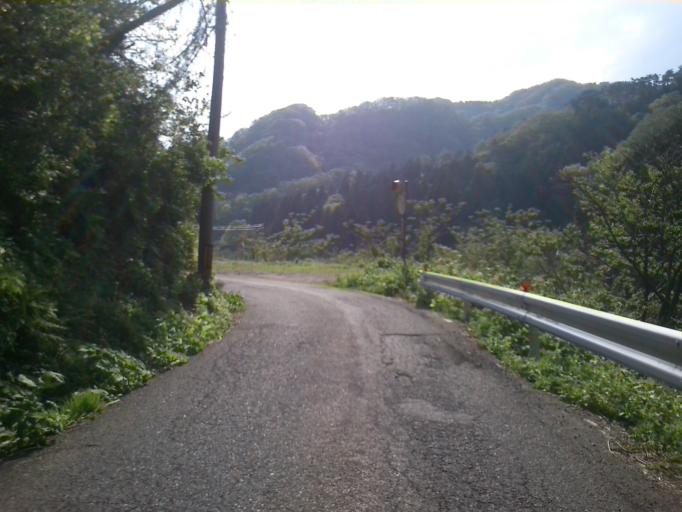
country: JP
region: Kyoto
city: Miyazu
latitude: 35.7001
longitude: 135.1818
